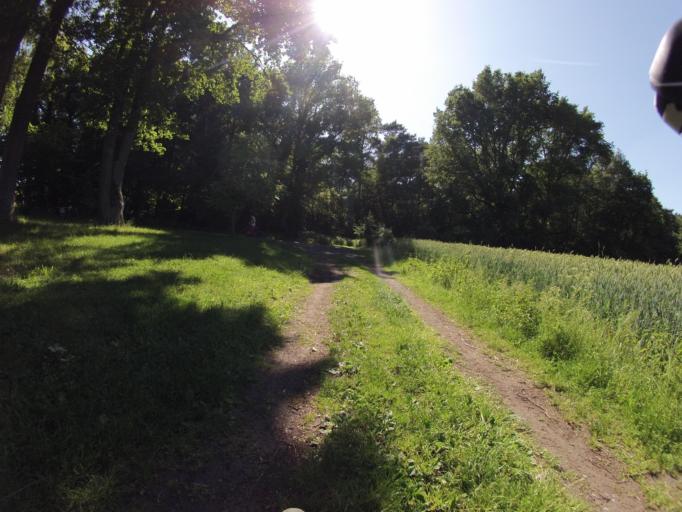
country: DE
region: North Rhine-Westphalia
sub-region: Regierungsbezirk Munster
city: Dreierwalde
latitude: 52.2639
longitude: 7.4753
